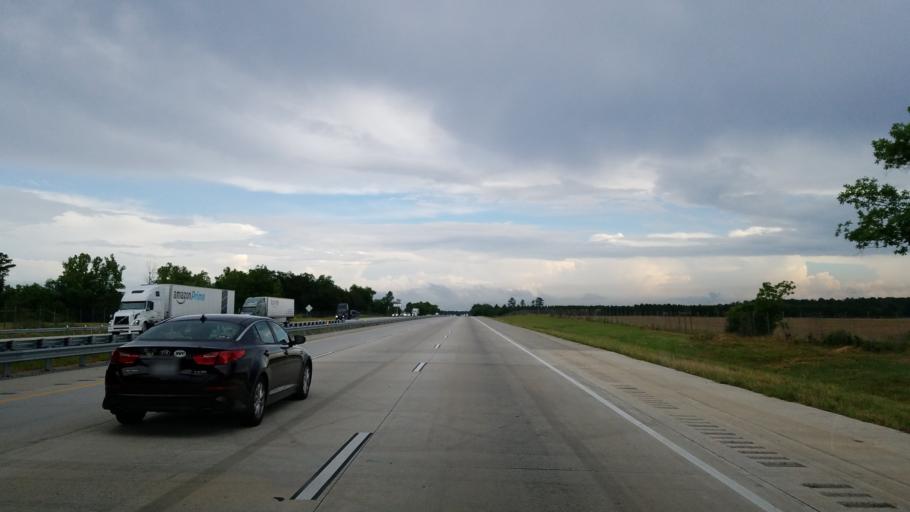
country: US
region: Georgia
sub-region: Dooly County
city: Vienna
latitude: 32.0598
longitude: -83.7637
